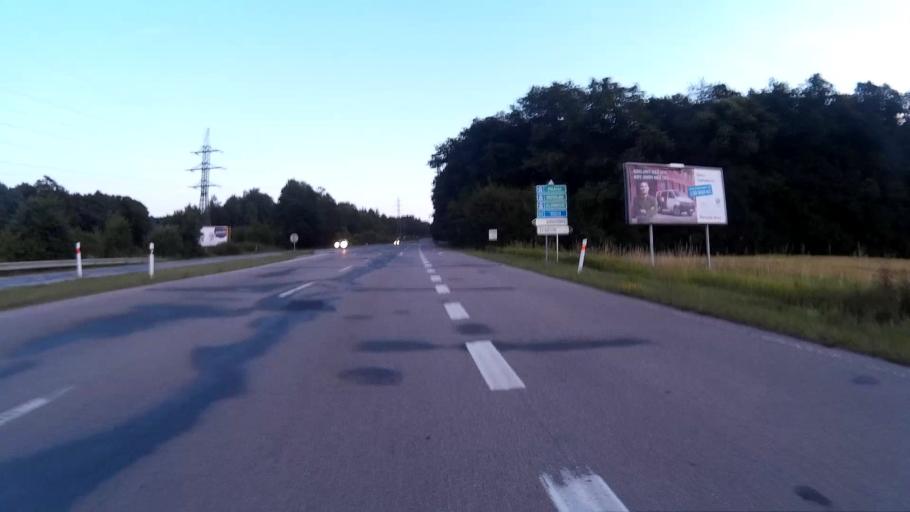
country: CZ
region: South Moravian
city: Troubsko
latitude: 49.2021
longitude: 16.5174
